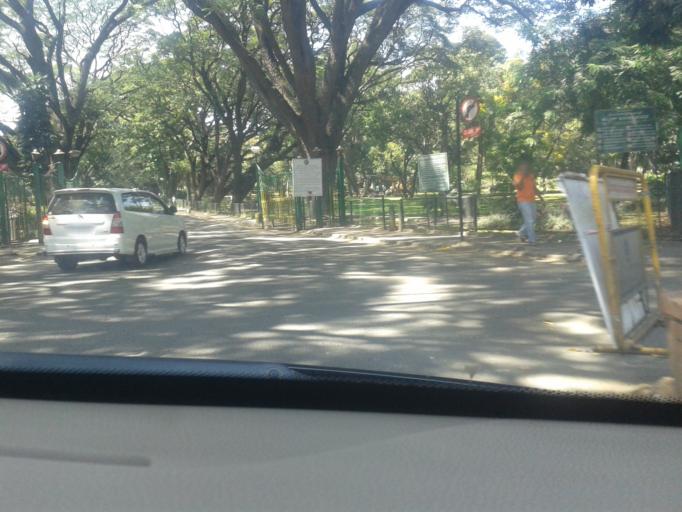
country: IN
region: Karnataka
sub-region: Bangalore Urban
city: Bangalore
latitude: 12.9723
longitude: 77.5939
